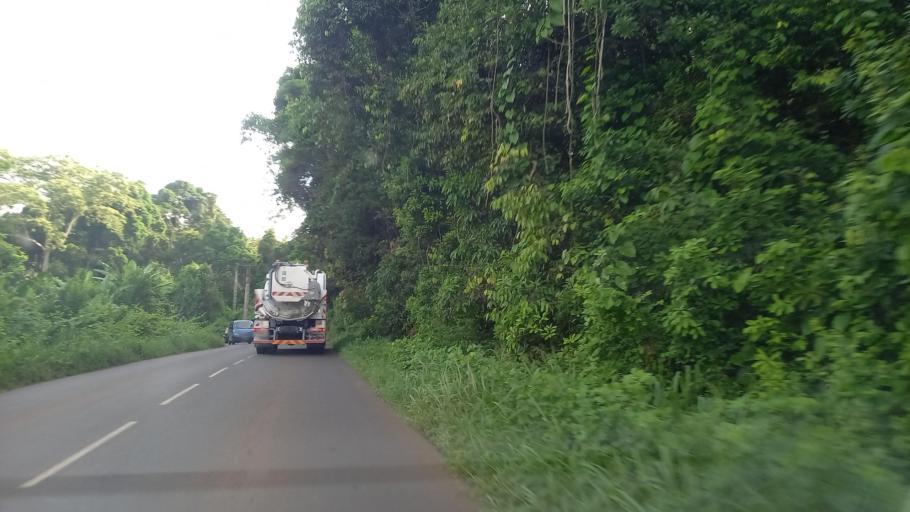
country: YT
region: Chiconi
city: Chiconi
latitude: -12.8098
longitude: 45.1277
